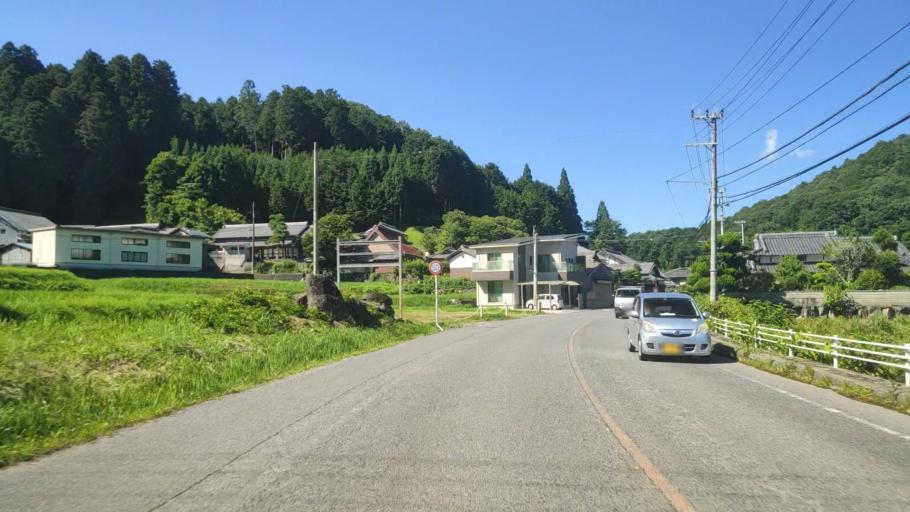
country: JP
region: Nara
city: Haibara-akanedai
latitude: 34.5807
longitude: 135.9688
